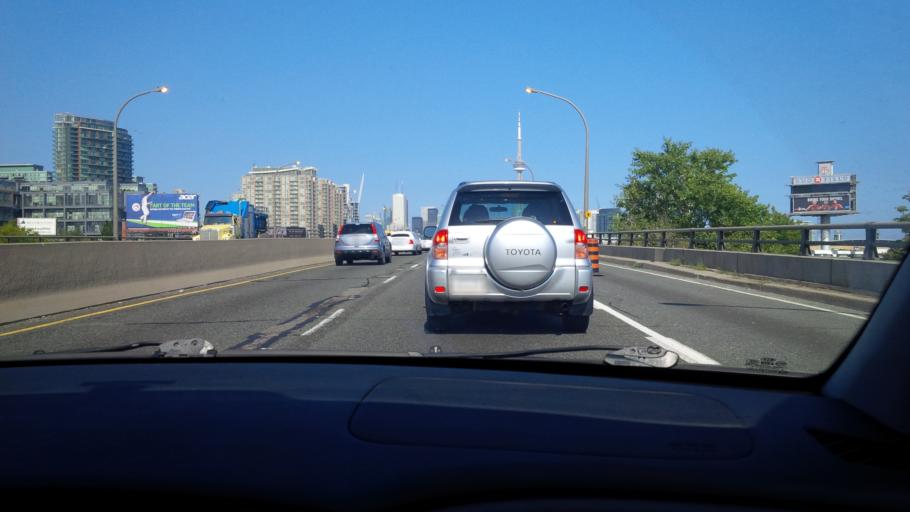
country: CA
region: Ontario
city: Toronto
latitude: 43.6349
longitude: -79.4216
